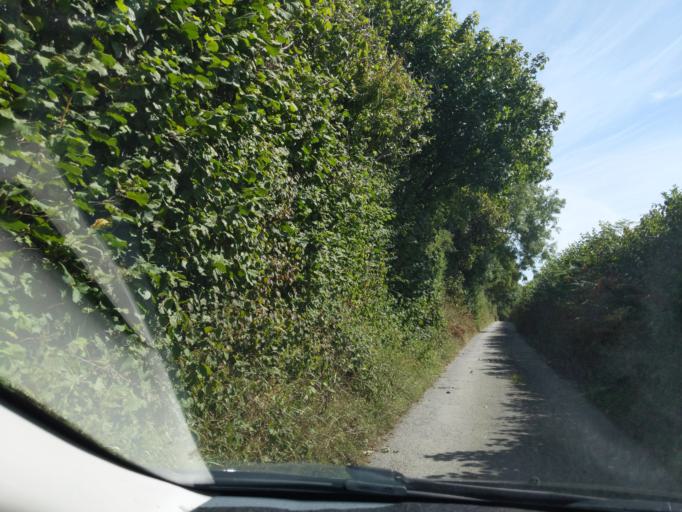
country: GB
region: England
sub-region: Devon
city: Plympton
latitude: 50.3775
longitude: -4.0439
